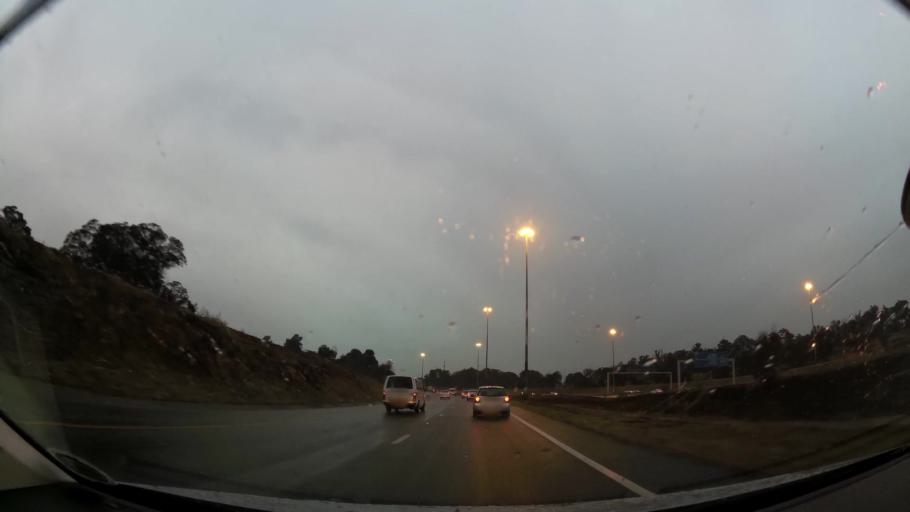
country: ZA
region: Gauteng
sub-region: City of Johannesburg Metropolitan Municipality
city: Johannesburg
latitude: -26.2603
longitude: 27.9683
